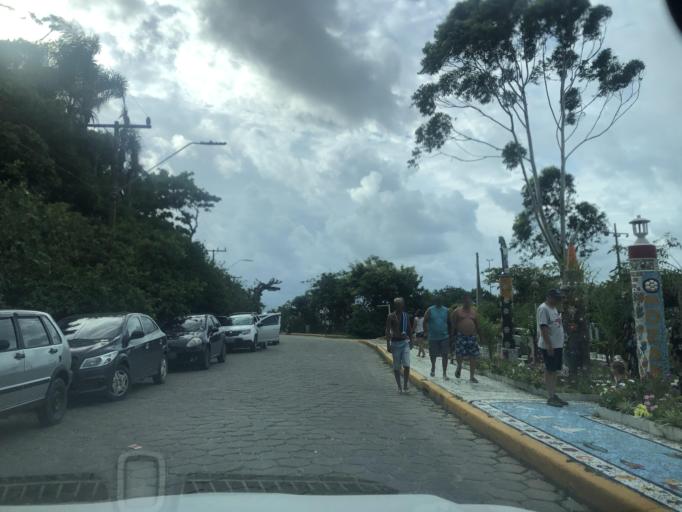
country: BR
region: Santa Catarina
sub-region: Sao Francisco Do Sul
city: Sao Francisco do Sul
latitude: -26.2203
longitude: -48.4999
